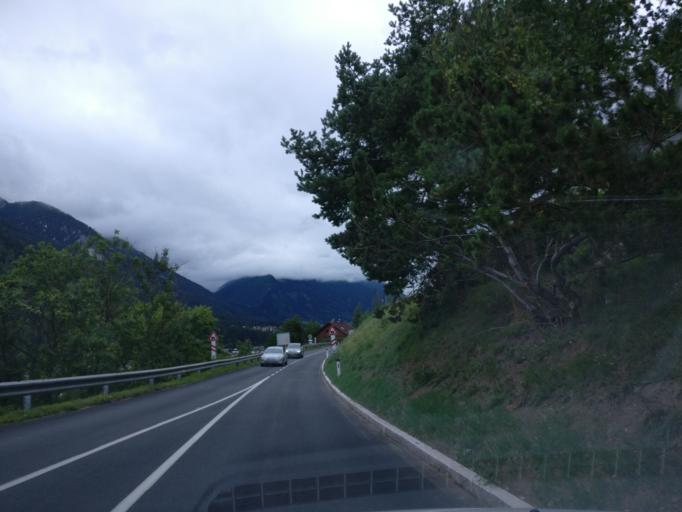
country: AT
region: Tyrol
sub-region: Politischer Bezirk Innsbruck Land
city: Fulpmes
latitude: 47.1578
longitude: 11.3546
